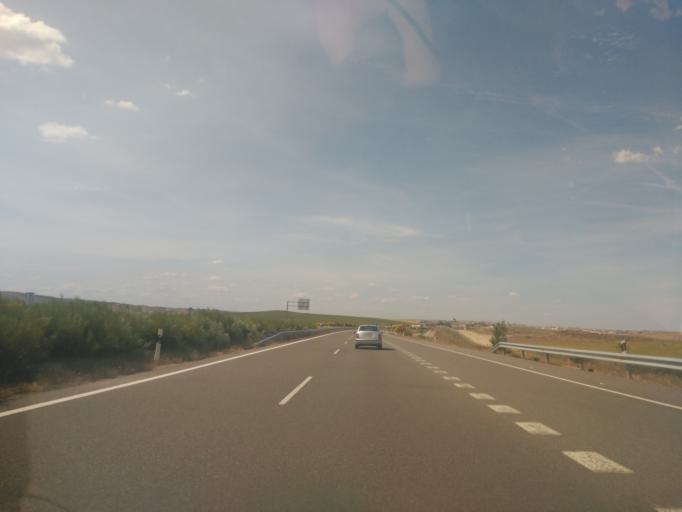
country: ES
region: Castille and Leon
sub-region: Provincia de Salamanca
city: Arapiles
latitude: 40.8978
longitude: -5.6613
